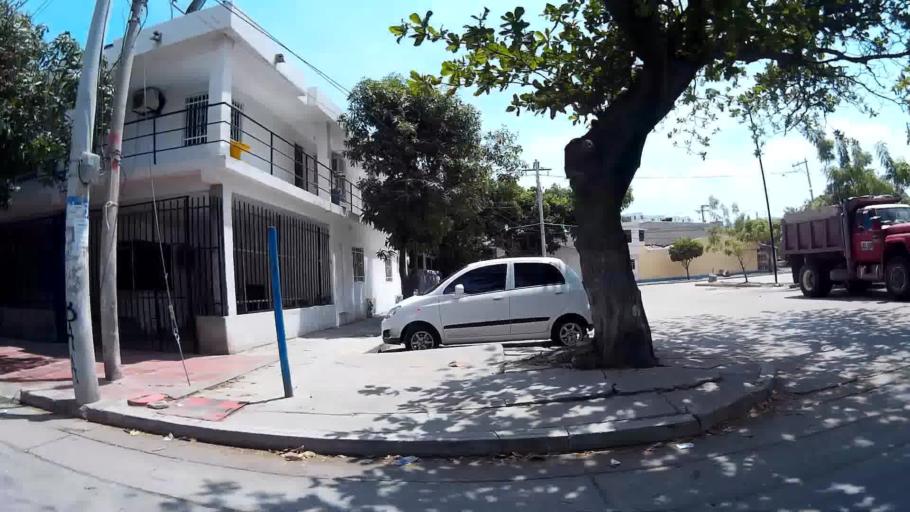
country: CO
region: Magdalena
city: Santa Marta
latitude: 11.2255
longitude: -74.1994
